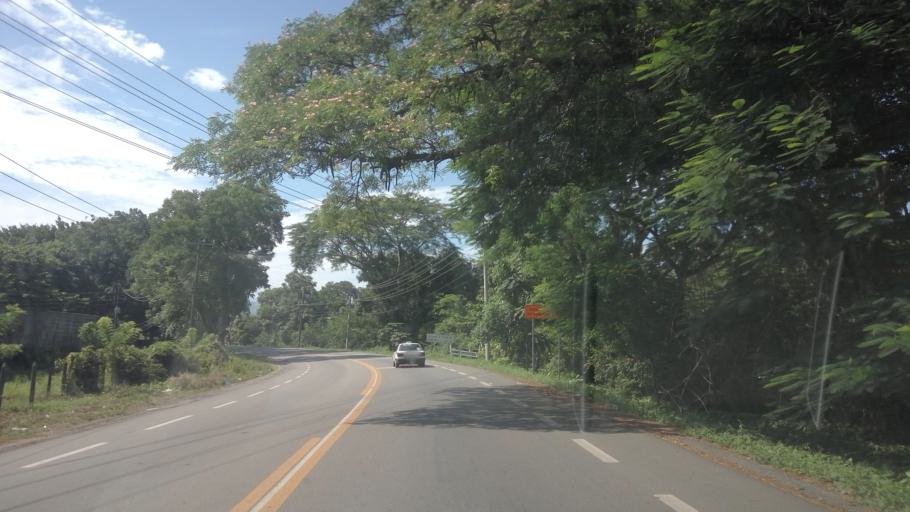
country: MX
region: Tabasco
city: Teapa
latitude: 17.5837
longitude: -92.9680
